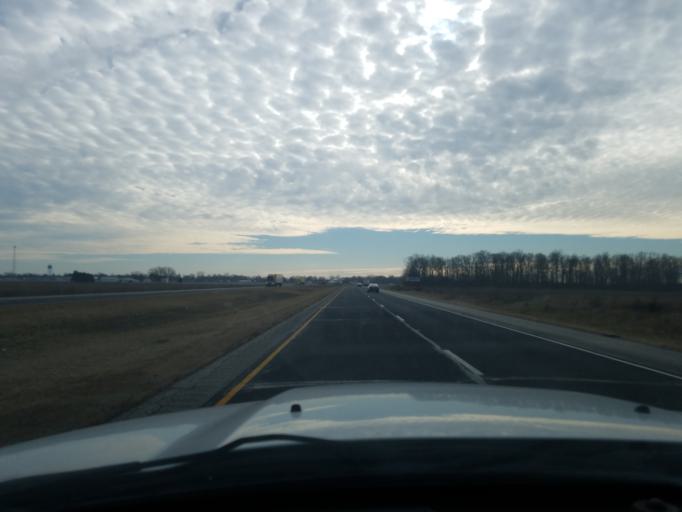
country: US
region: Indiana
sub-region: Huntington County
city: Markle
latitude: 40.8411
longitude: -85.3448
